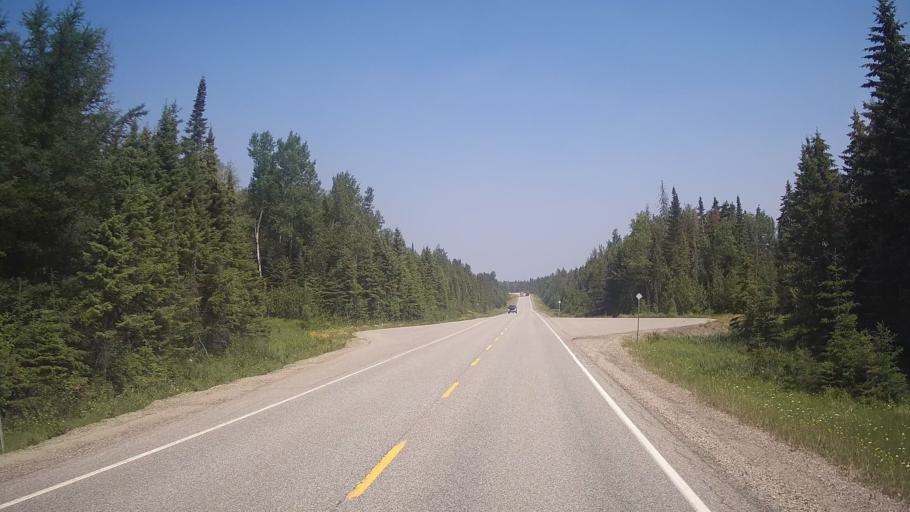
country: CA
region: Ontario
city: Timmins
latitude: 48.0928
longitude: -81.5936
